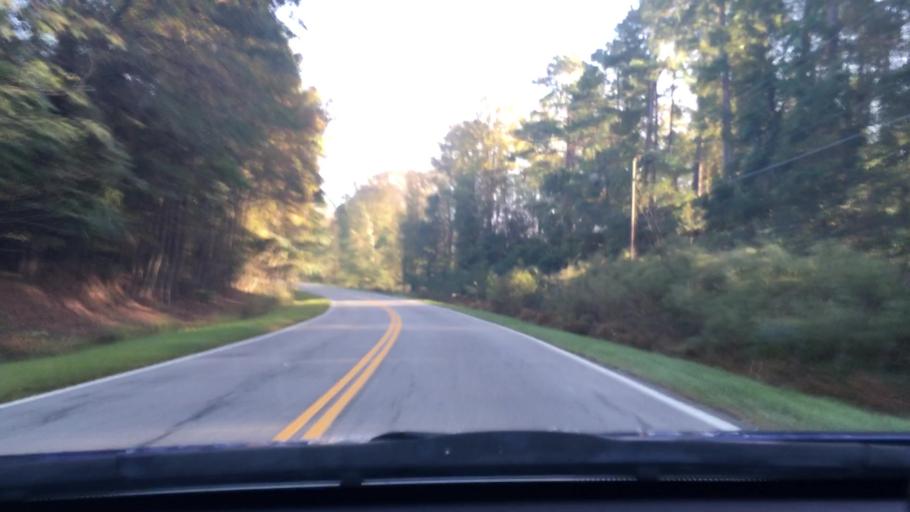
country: US
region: South Carolina
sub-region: Sumter County
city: East Sumter
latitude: 33.9616
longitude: -80.3025
